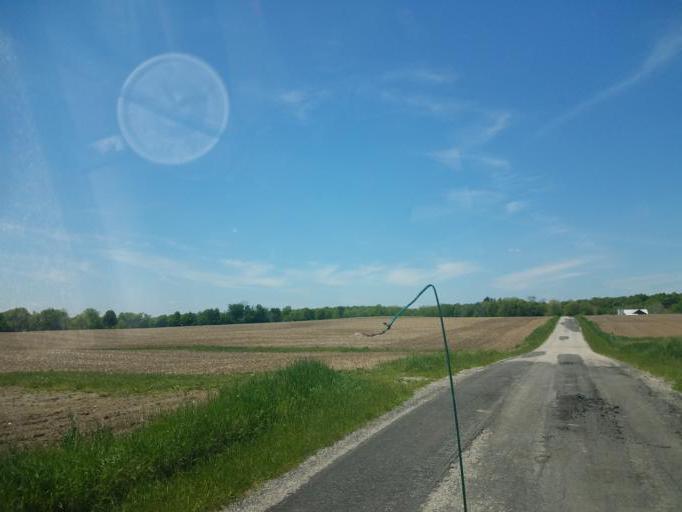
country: US
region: Ohio
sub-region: Ashland County
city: Ashland
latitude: 40.9469
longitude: -82.2730
